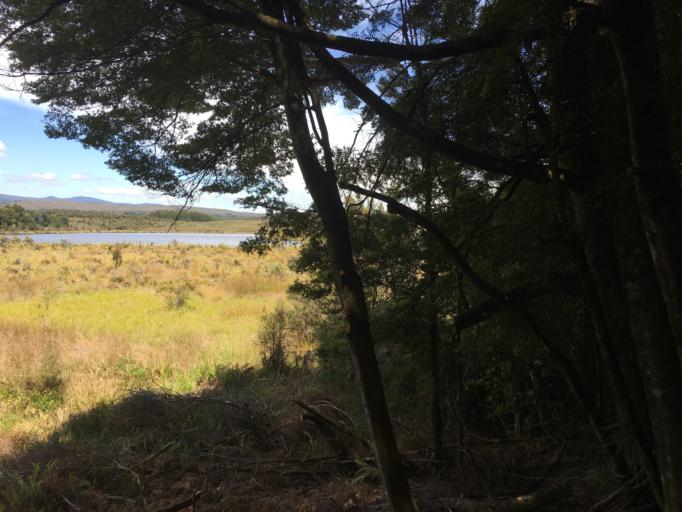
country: NZ
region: Southland
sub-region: Southland District
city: Te Anau
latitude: -45.1995
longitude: 167.8249
